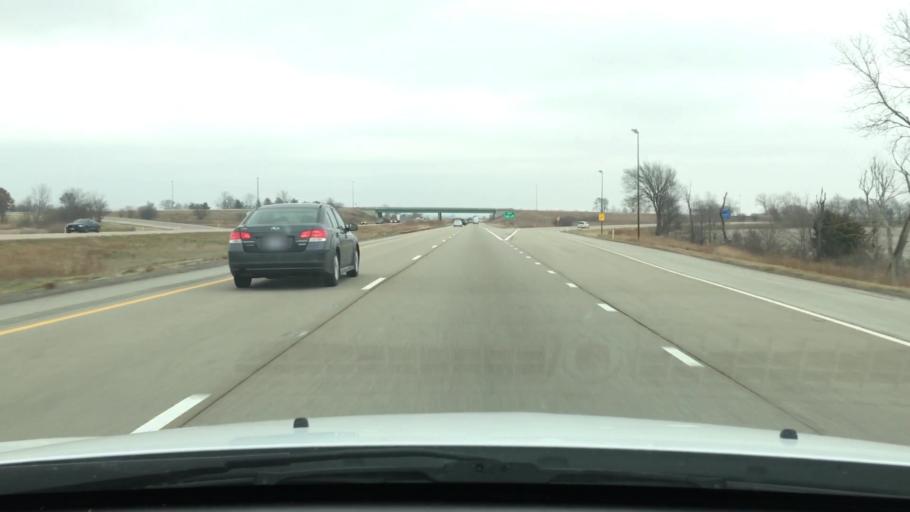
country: US
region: Illinois
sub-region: Logan County
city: Atlanta
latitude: 40.2563
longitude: -89.2236
